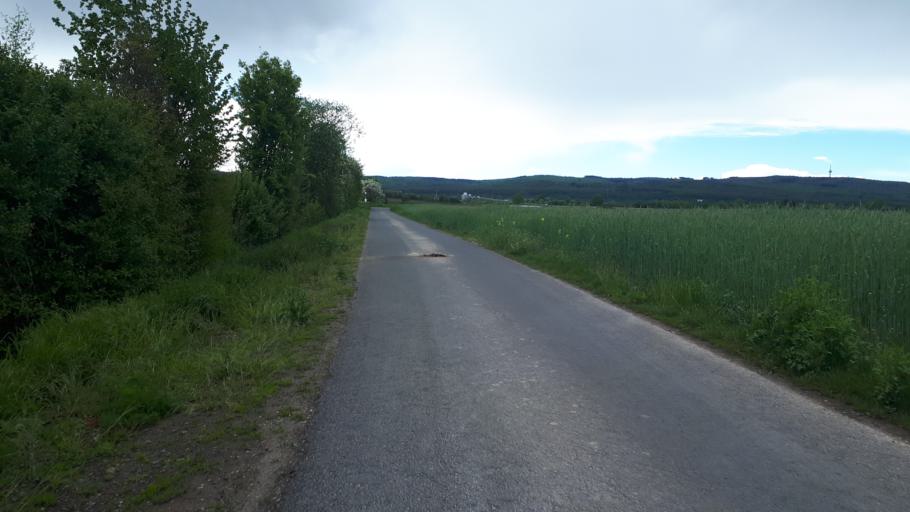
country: DE
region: Hesse
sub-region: Regierungsbezirk Darmstadt
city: Rosbach vor der Hohe
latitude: 50.2886
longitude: 8.7176
